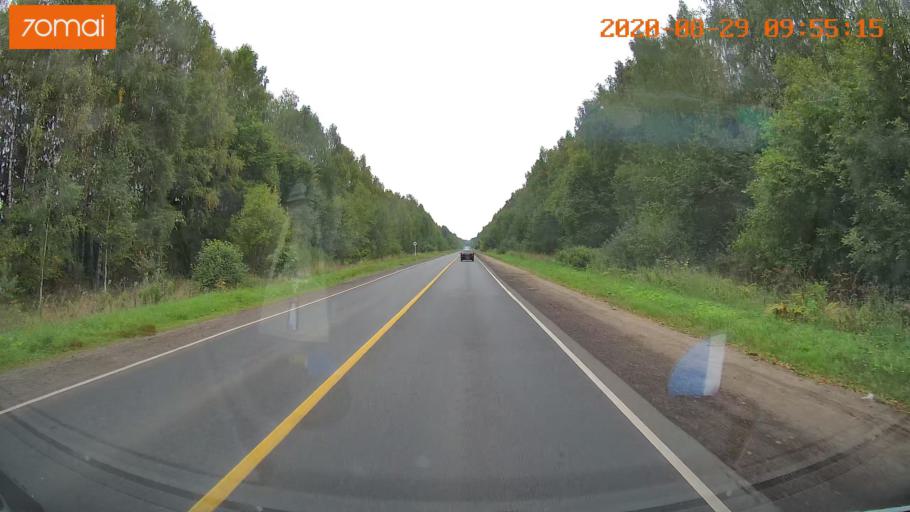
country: RU
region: Ivanovo
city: Zarechnyy
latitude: 57.4226
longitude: 42.2585
